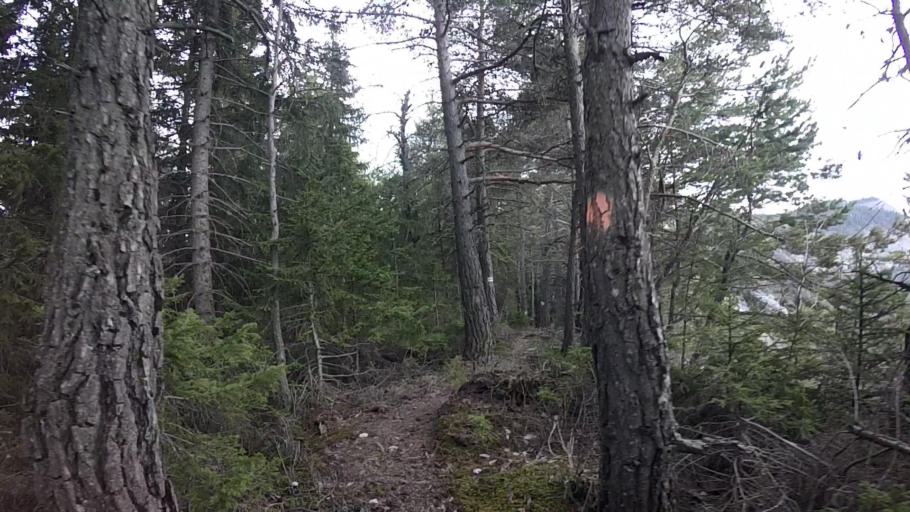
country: FR
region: Provence-Alpes-Cote d'Azur
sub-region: Departement des Alpes-de-Haute-Provence
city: Seyne-les-Alpes
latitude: 44.3221
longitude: 6.3364
